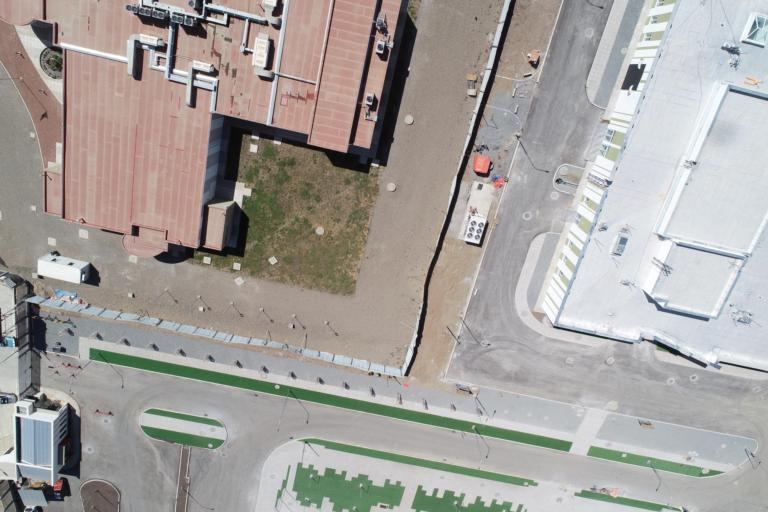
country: BO
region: La Paz
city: La Paz
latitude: -16.5937
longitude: -68.2150
